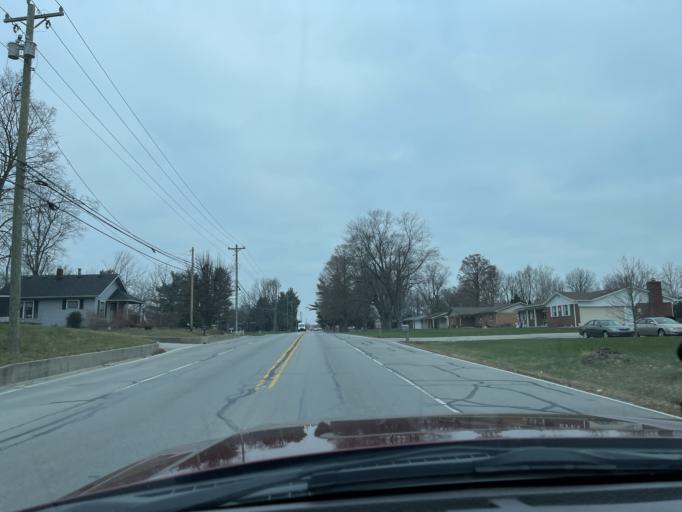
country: US
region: Indiana
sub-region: Hendricks County
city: Avon
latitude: 39.7726
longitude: -86.3996
